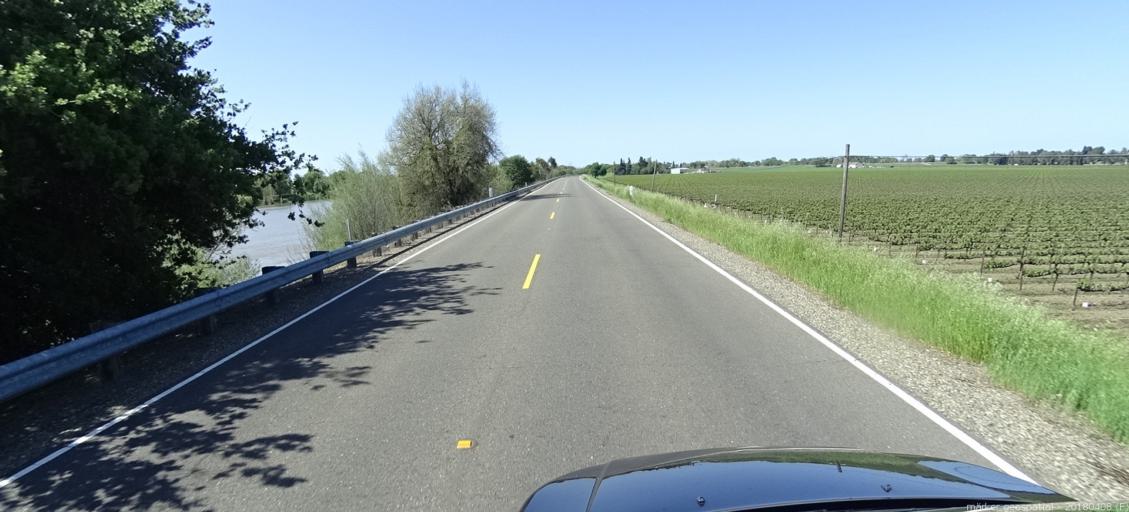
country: US
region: California
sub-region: Sacramento County
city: Parkway
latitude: 38.4227
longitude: -121.5261
